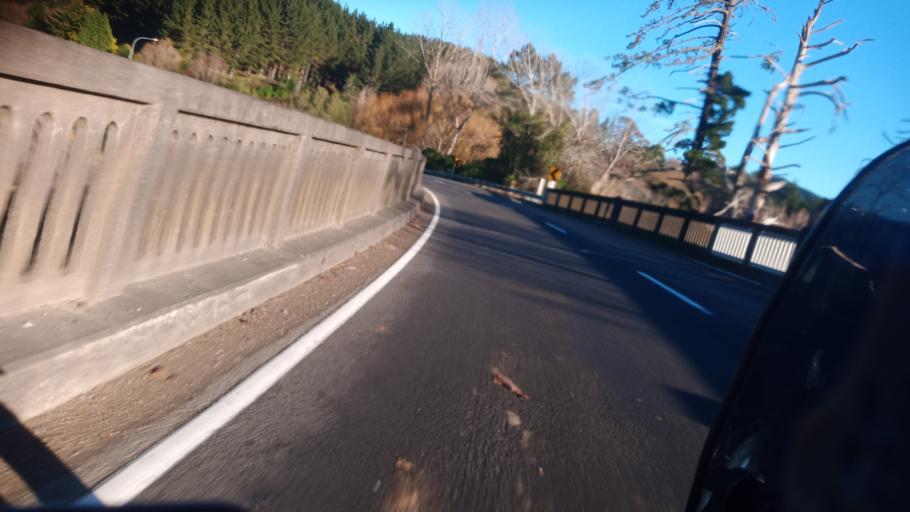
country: NZ
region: Hawke's Bay
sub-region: Wairoa District
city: Wairoa
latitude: -39.0146
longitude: 177.3356
